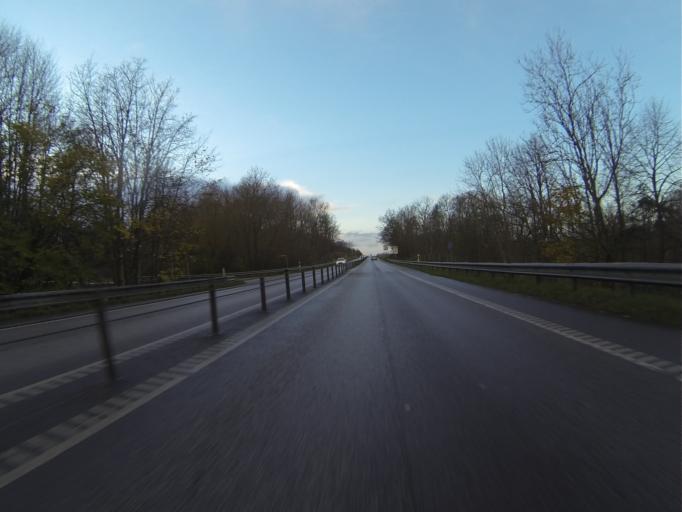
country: SE
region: Skane
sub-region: Trelleborgs Kommun
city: Anderslov
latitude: 55.5105
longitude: 13.3158
